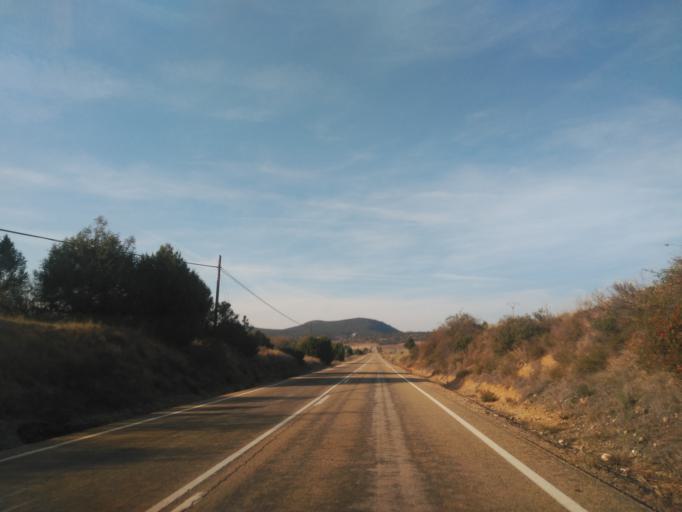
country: ES
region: Castille and Leon
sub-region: Provincia de Soria
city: Ucero
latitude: 41.6972
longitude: -3.0434
